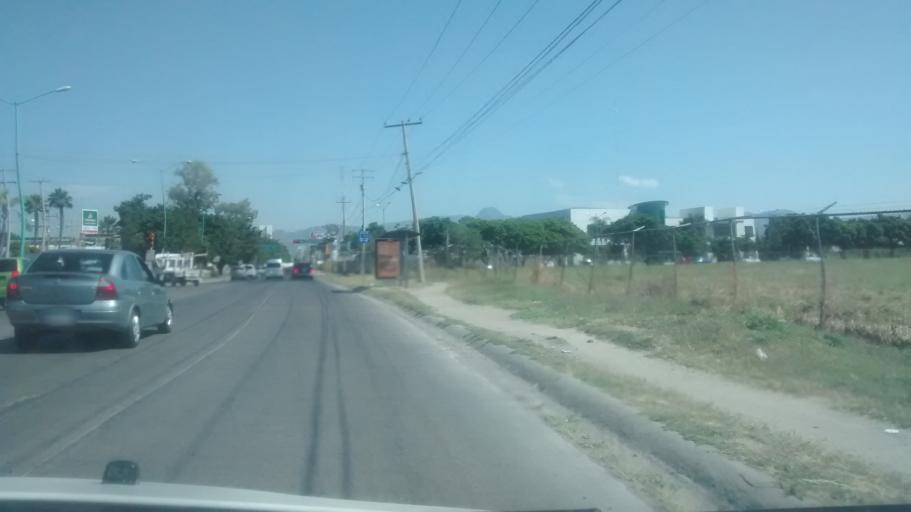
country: MX
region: Guanajuato
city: Leon
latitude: 21.1026
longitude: -101.6601
